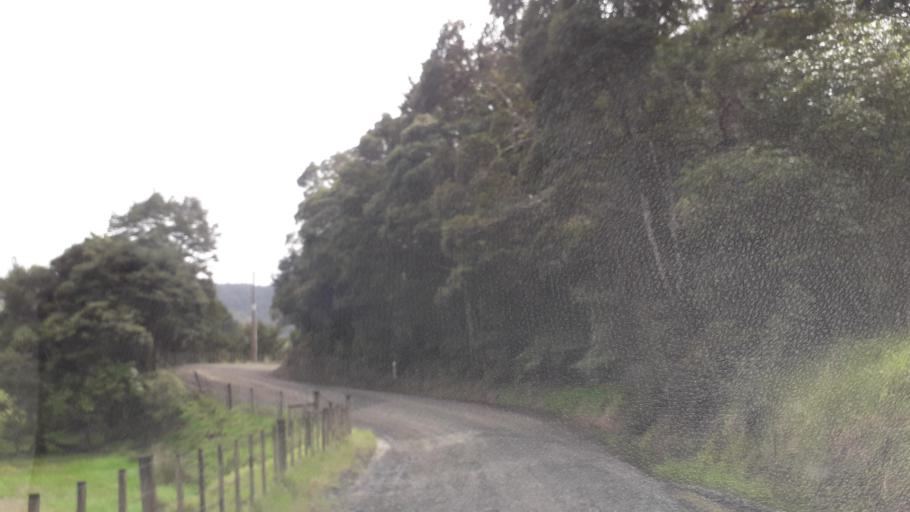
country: NZ
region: Northland
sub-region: Far North District
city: Kaitaia
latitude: -35.2310
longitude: 173.2646
